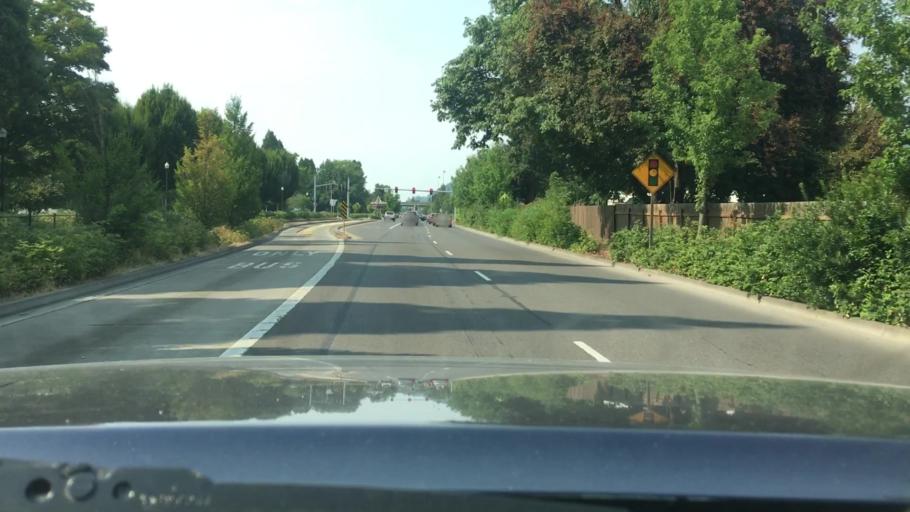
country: US
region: Oregon
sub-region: Lane County
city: Springfield
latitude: 44.0552
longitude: -123.0234
